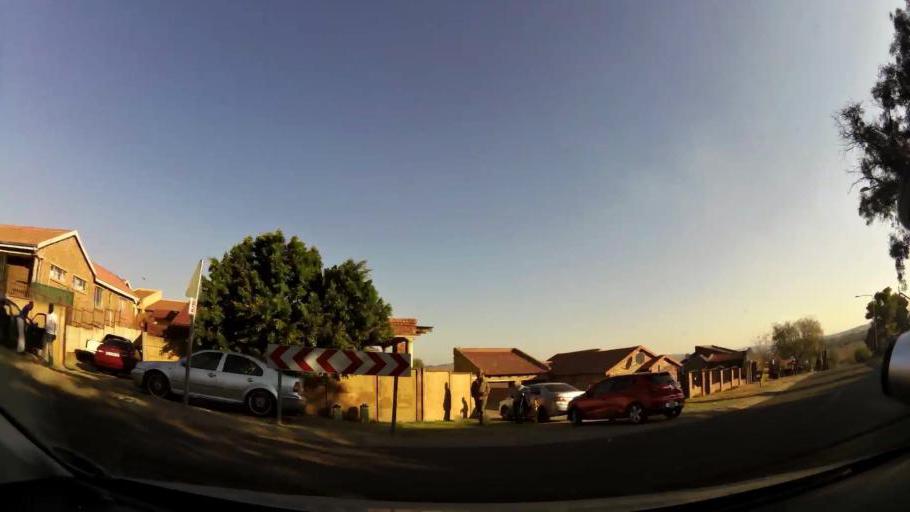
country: ZA
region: Gauteng
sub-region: City of Tshwane Metropolitan Municipality
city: Pretoria
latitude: -25.7328
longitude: 28.1200
